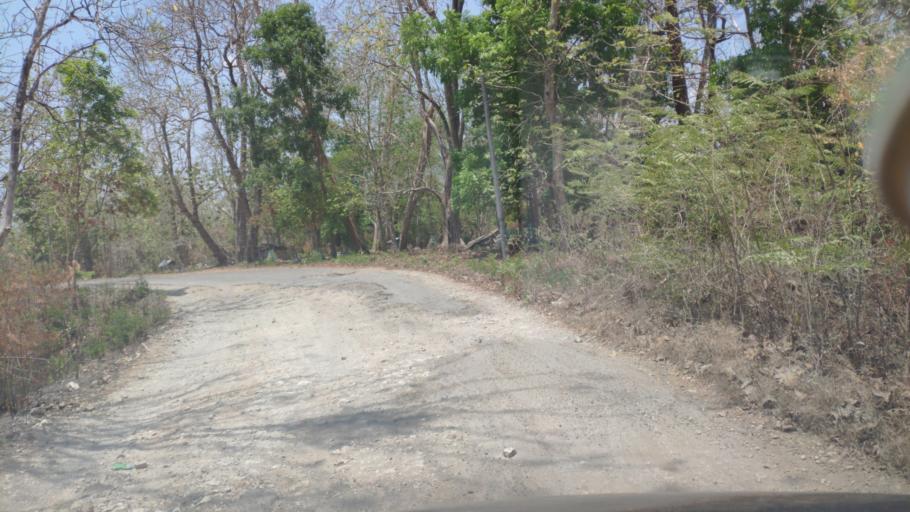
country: ID
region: Central Java
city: Randublatung
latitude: -7.2543
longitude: 111.3795
